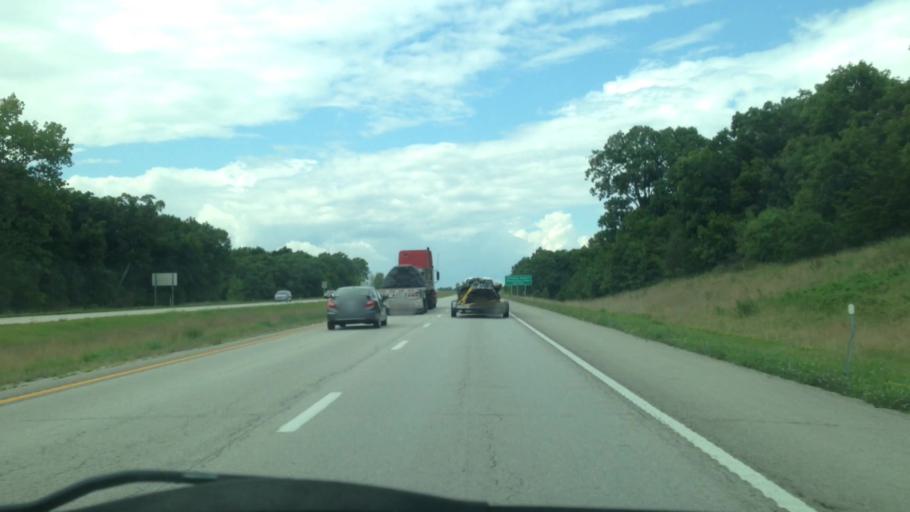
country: US
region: Missouri
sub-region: Pike County
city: Bowling Green
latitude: 39.3651
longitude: -91.2094
